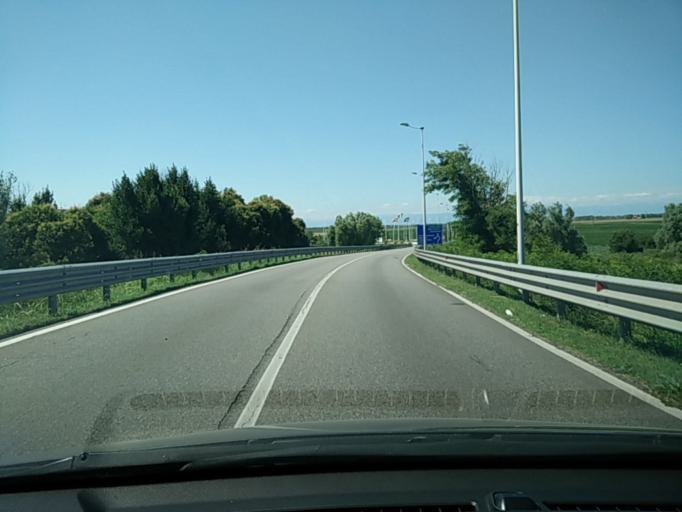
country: IT
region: Veneto
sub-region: Provincia di Venezia
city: Caorle
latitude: 45.6066
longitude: 12.8785
